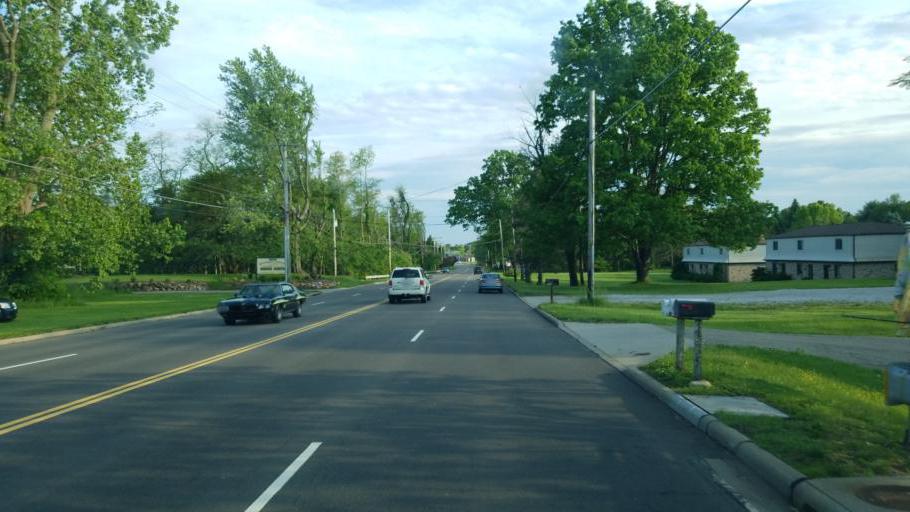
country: US
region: Ohio
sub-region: Stark County
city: Uniontown
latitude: 40.9669
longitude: -81.4083
